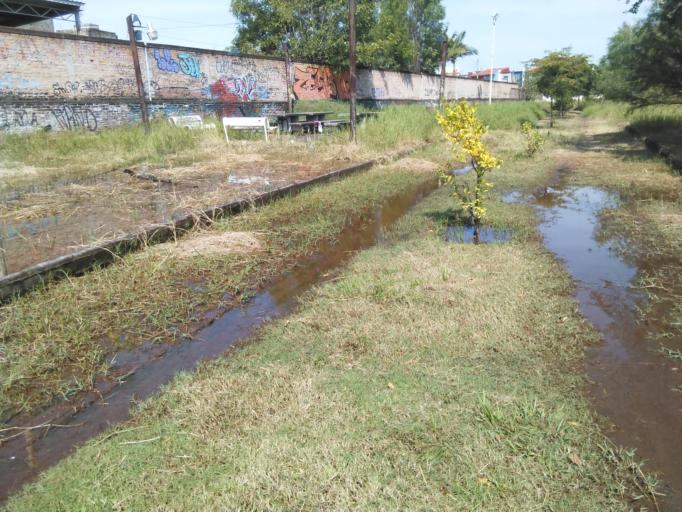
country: MX
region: Nayarit
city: Tepic
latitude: 21.4849
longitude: -104.8592
